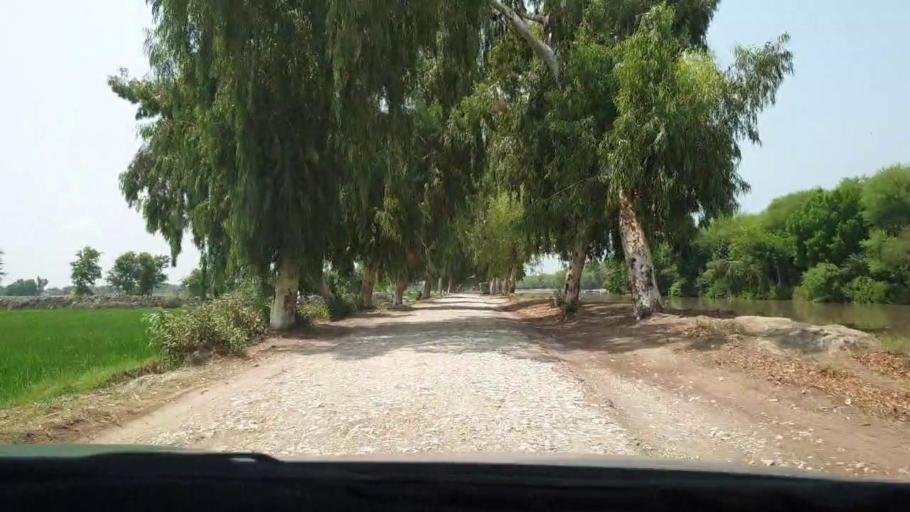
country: PK
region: Sindh
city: Dokri
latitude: 27.3041
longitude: 68.0935
